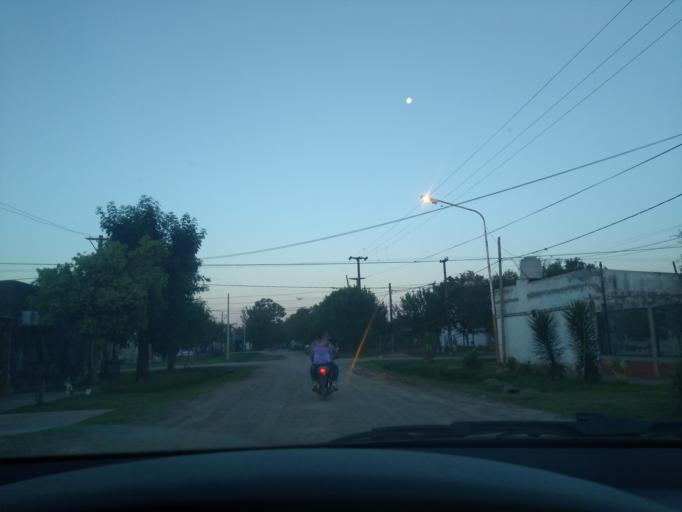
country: AR
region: Chaco
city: Barranqueras
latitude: -27.4745
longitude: -58.9320
